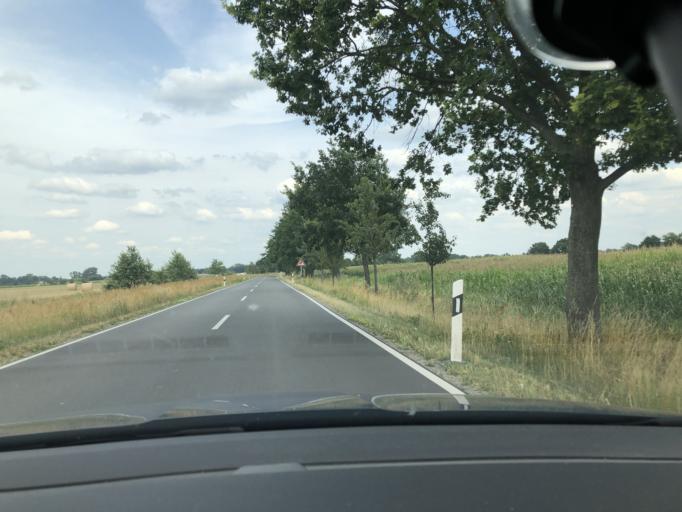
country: DE
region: Brandenburg
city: Schlepzig
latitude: 52.0721
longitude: 13.8634
